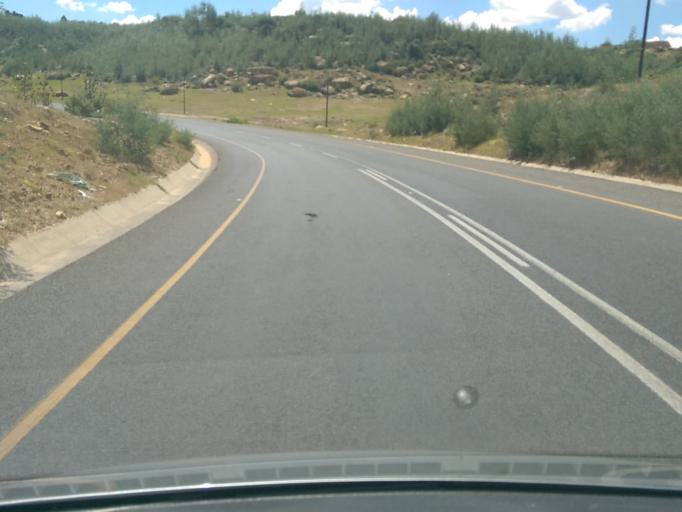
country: LS
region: Maseru
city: Maseru
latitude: -29.3955
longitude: 27.5297
